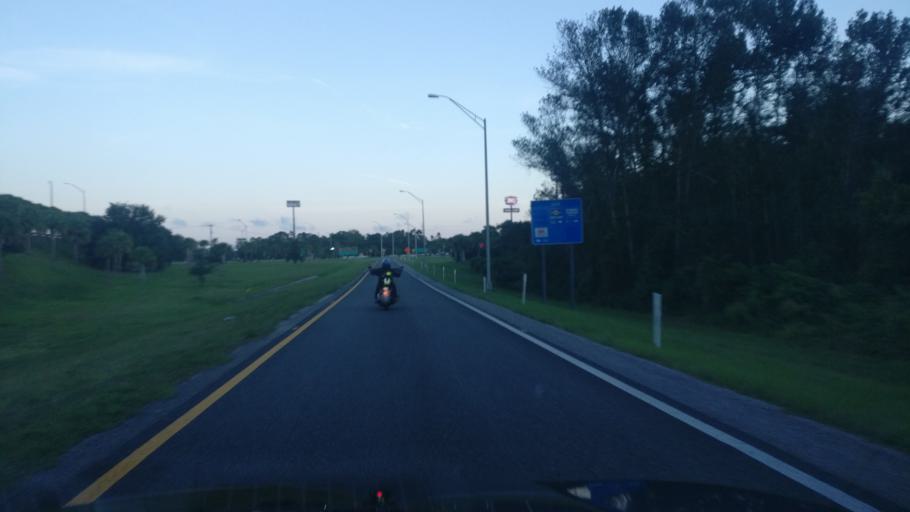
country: US
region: Florida
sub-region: Flagler County
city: Palm Coast
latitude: 29.6631
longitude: -81.2897
